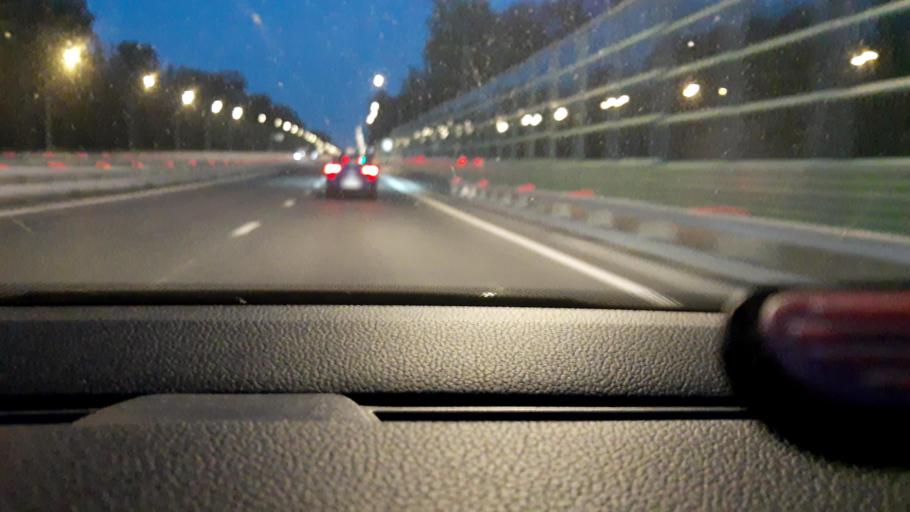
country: RU
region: Moskovskaya
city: Moskovskiy
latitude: 55.5784
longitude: 37.3809
